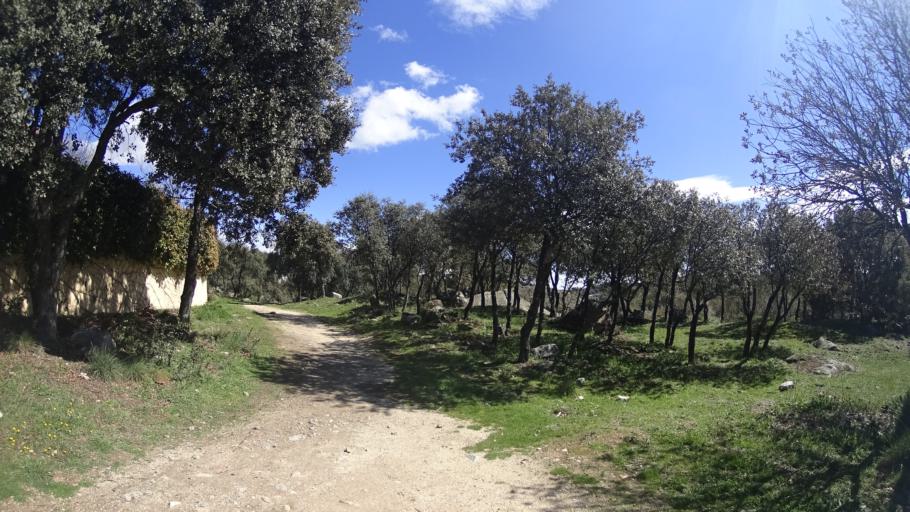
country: ES
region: Madrid
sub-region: Provincia de Madrid
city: Torrelodones
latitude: 40.5705
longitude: -3.9483
